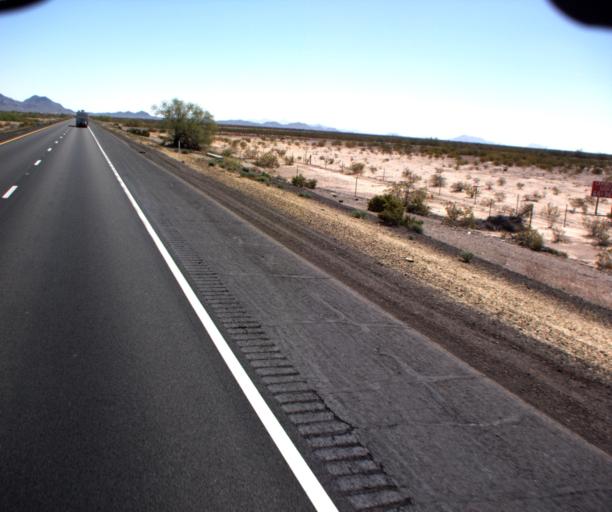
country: US
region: Arizona
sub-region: La Paz County
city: Salome
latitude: 33.6258
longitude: -113.7345
